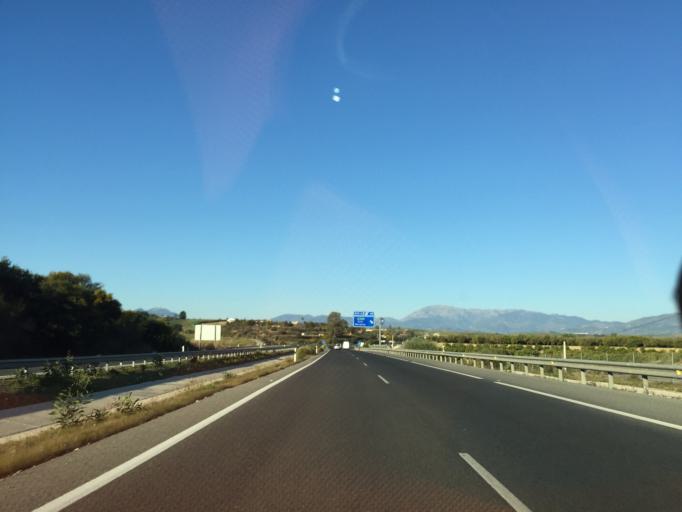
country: ES
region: Andalusia
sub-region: Provincia de Malaga
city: Cartama
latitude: 36.7203
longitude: -4.6810
